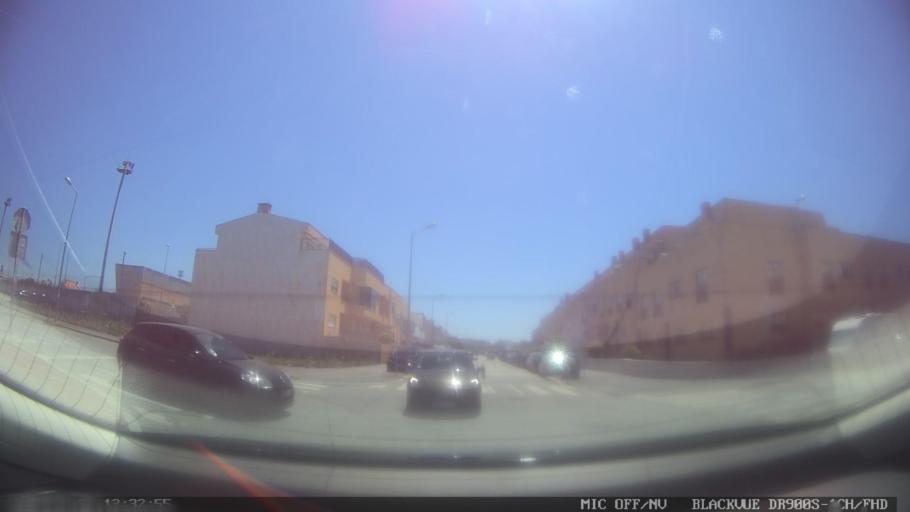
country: PT
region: Porto
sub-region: Matosinhos
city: Lavra
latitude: 41.2542
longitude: -8.7209
